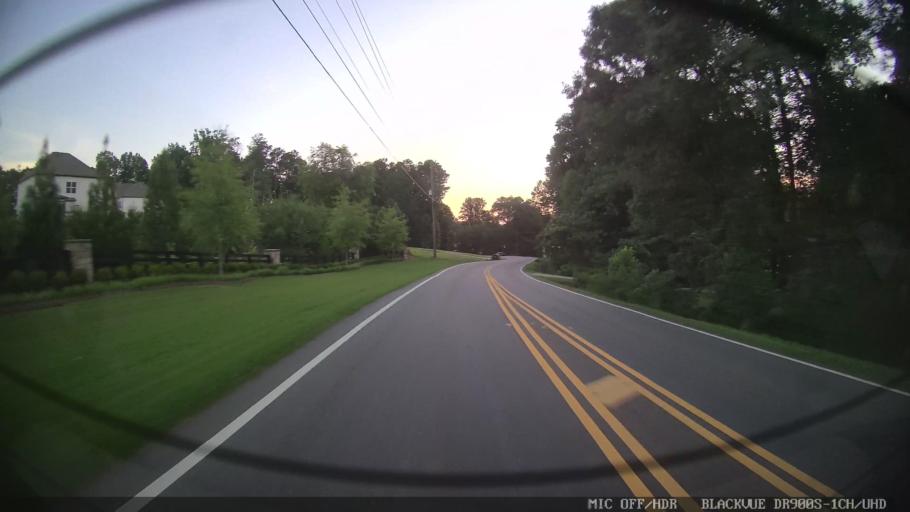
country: US
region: Georgia
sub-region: Forsyth County
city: Cumming
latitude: 34.2901
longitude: -84.1676
